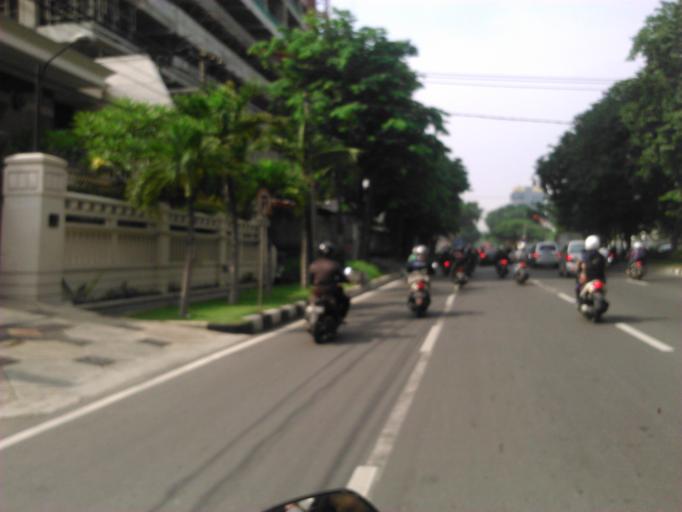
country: ID
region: East Java
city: Mulyorejo
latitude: -7.2794
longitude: 112.7810
